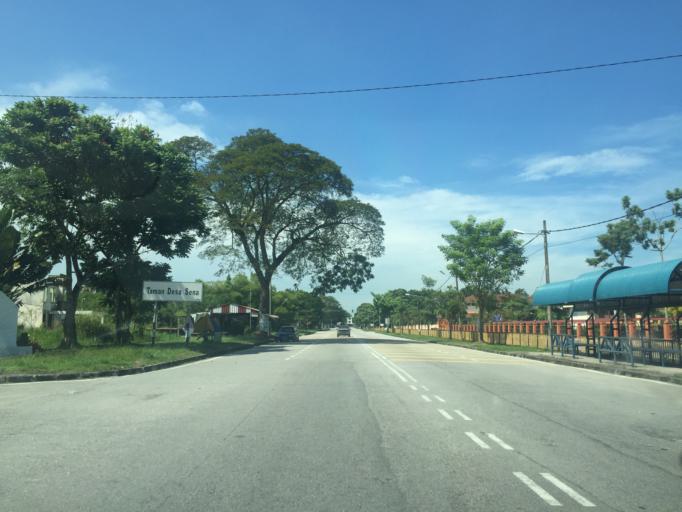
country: MY
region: Penang
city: Tasek Glugor
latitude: 5.4890
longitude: 100.4633
